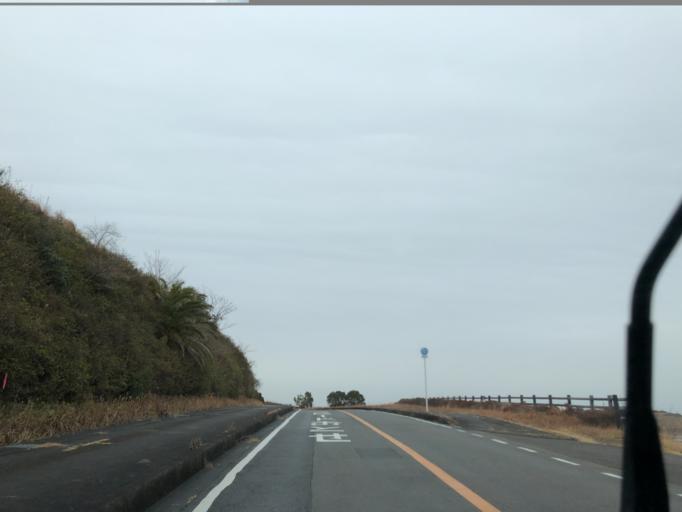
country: JP
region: Wakayama
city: Tanabe
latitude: 33.6657
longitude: 135.3588
